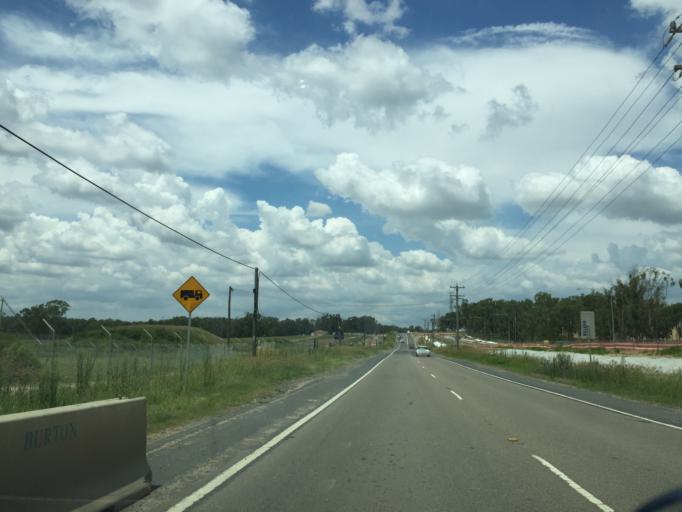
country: AU
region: New South Wales
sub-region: Blacktown
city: Hassall Grove
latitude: -33.7079
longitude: 150.8397
